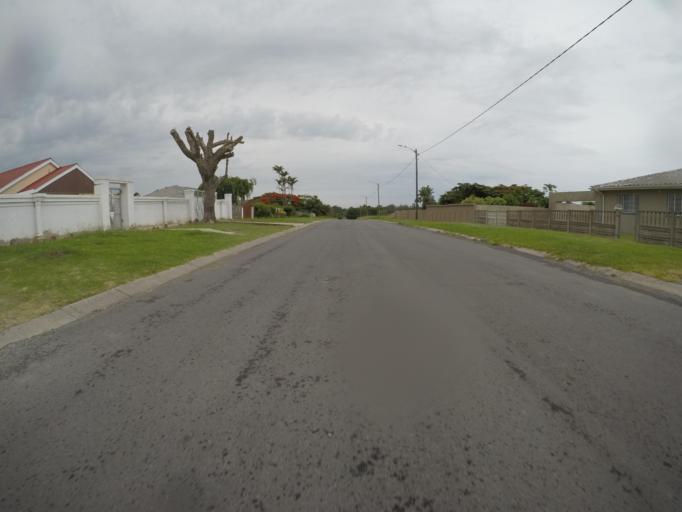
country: ZA
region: Eastern Cape
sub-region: Buffalo City Metropolitan Municipality
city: East London
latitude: -32.9667
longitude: 27.8338
